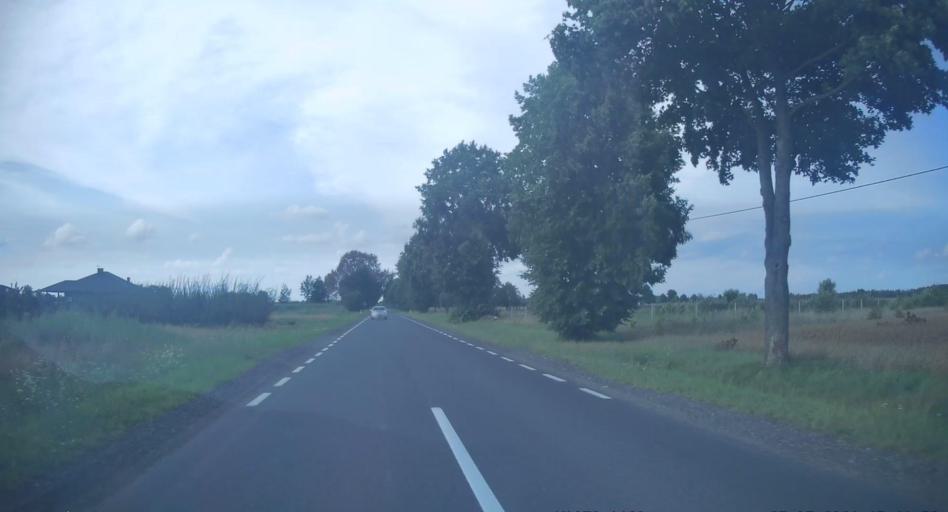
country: PL
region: Lodz Voivodeship
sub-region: Powiat rawski
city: Rawa Mazowiecka
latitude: 51.6895
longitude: 20.2670
